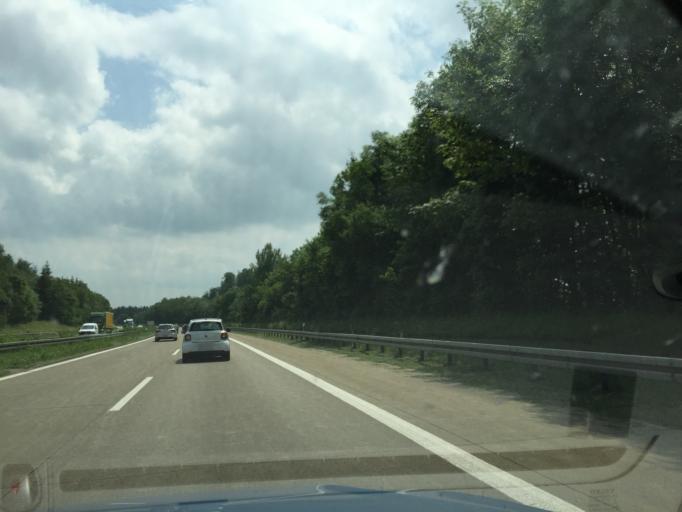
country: DE
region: Baden-Wuerttemberg
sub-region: Regierungsbezirk Stuttgart
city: Westhausen
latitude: 48.8456
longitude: 10.1974
